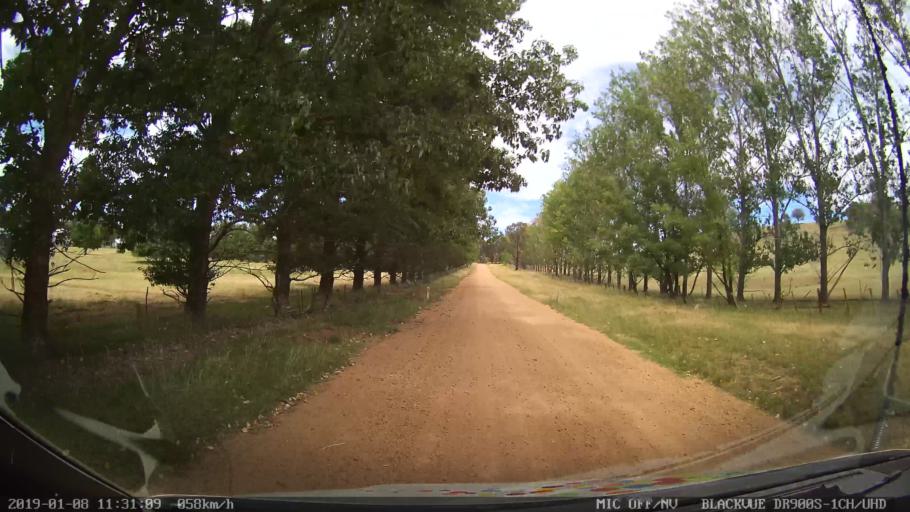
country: AU
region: New South Wales
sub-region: Guyra
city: Guyra
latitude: -30.3111
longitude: 151.5395
